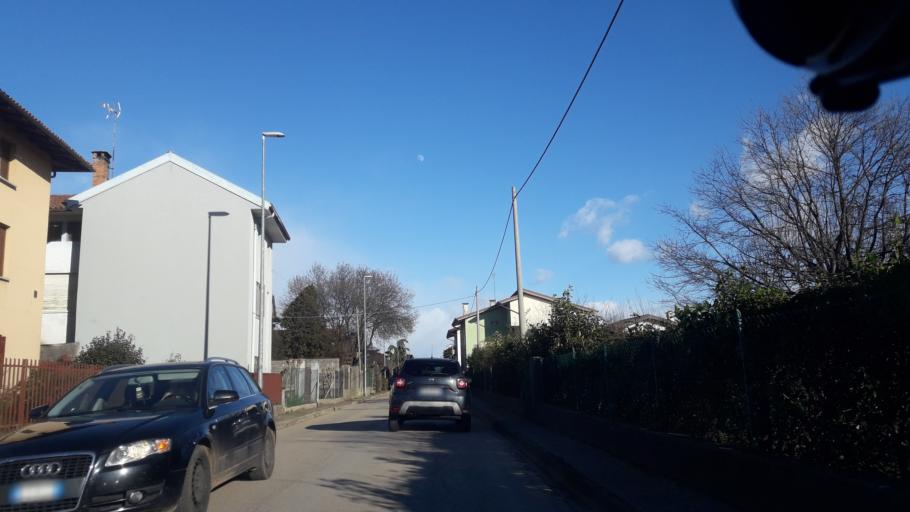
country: IT
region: Friuli Venezia Giulia
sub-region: Provincia di Udine
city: Martignacco
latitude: 46.0751
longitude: 13.1406
